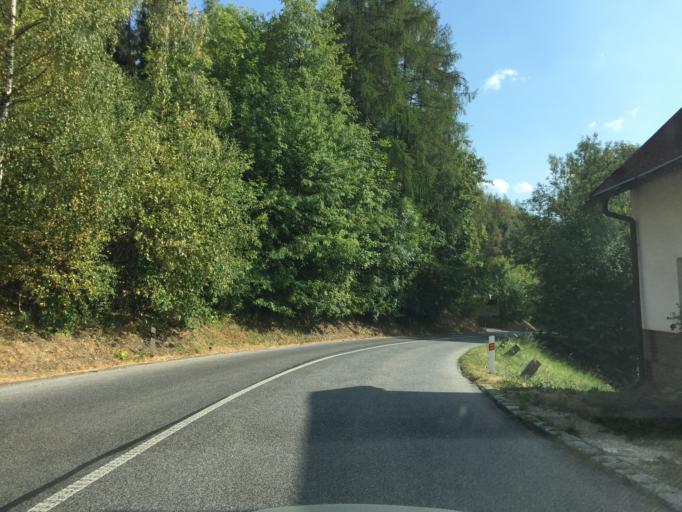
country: CZ
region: Liberecky
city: Mala Skala
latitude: 50.6558
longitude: 15.1608
